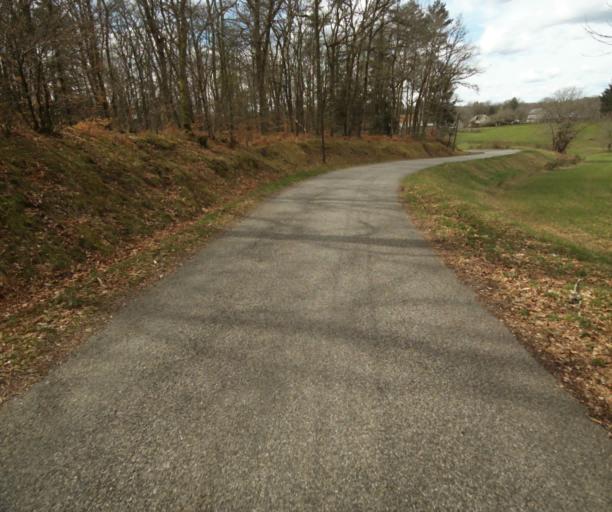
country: FR
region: Limousin
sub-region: Departement de la Correze
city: Argentat
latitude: 45.2229
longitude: 1.9216
